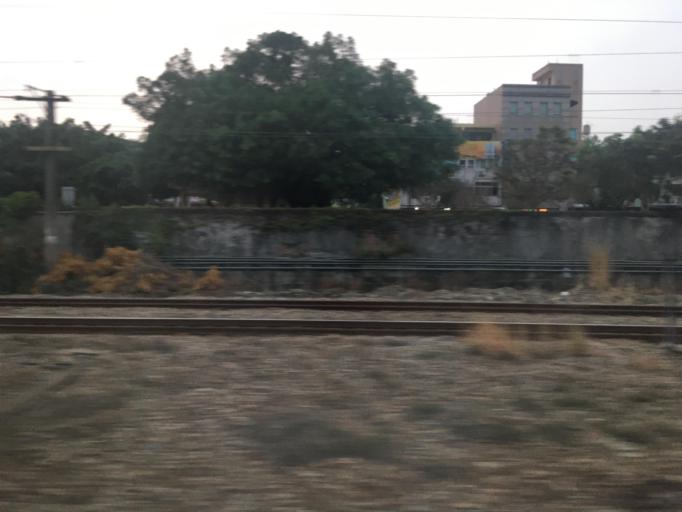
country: TW
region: Taiwan
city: Fengshan
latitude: 22.6569
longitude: 120.4214
